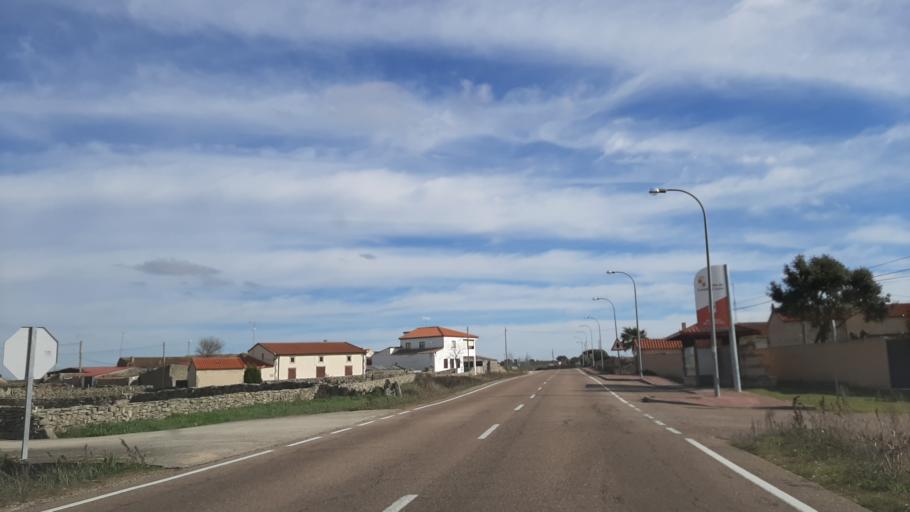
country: ES
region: Castille and Leon
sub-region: Provincia de Salamanca
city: Villaseco de los Reyes
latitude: 41.1638
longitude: -6.1848
